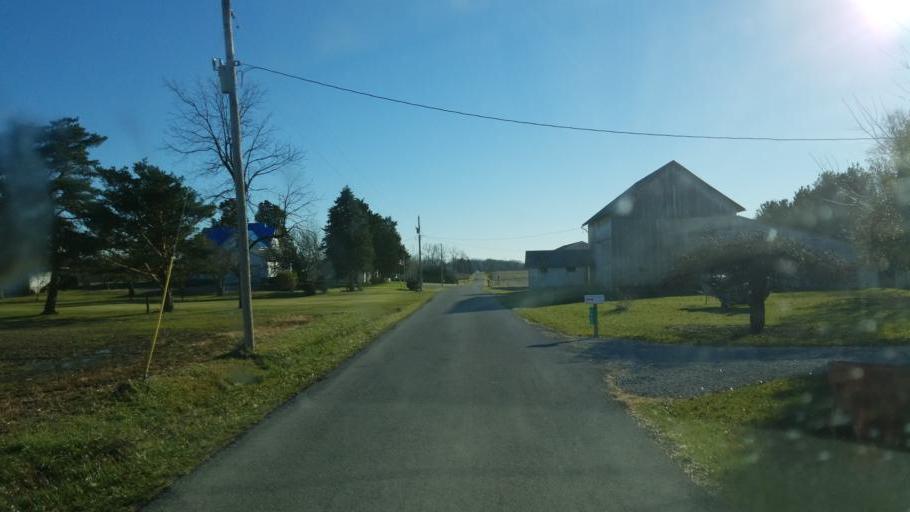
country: US
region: Ohio
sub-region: Morrow County
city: Cardington
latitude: 40.5041
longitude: -82.9488
